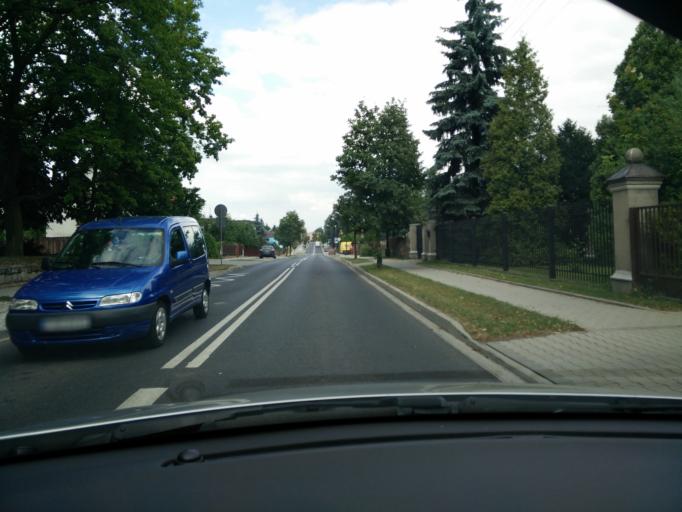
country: PL
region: Greater Poland Voivodeship
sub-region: Powiat sredzki
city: Sroda Wielkopolska
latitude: 52.2272
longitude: 17.2861
